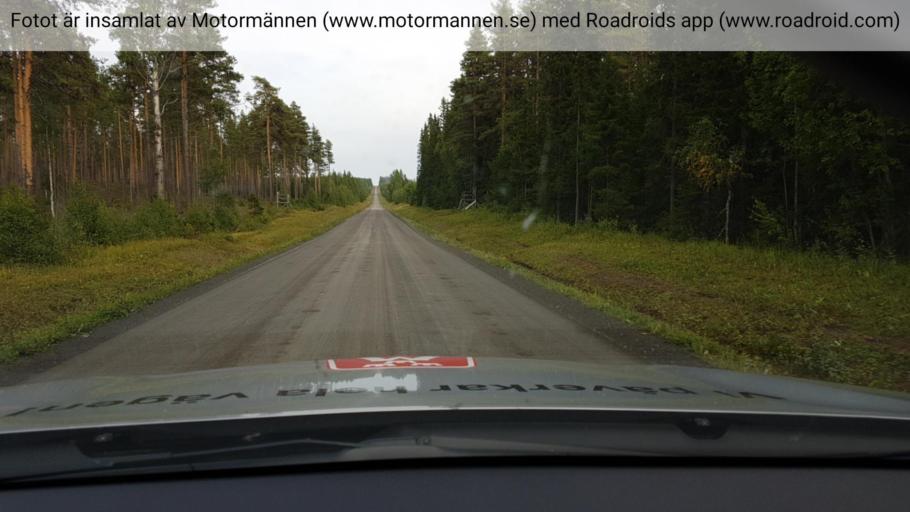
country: SE
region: Jaemtland
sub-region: OEstersunds Kommun
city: Lit
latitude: 63.6795
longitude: 14.7695
